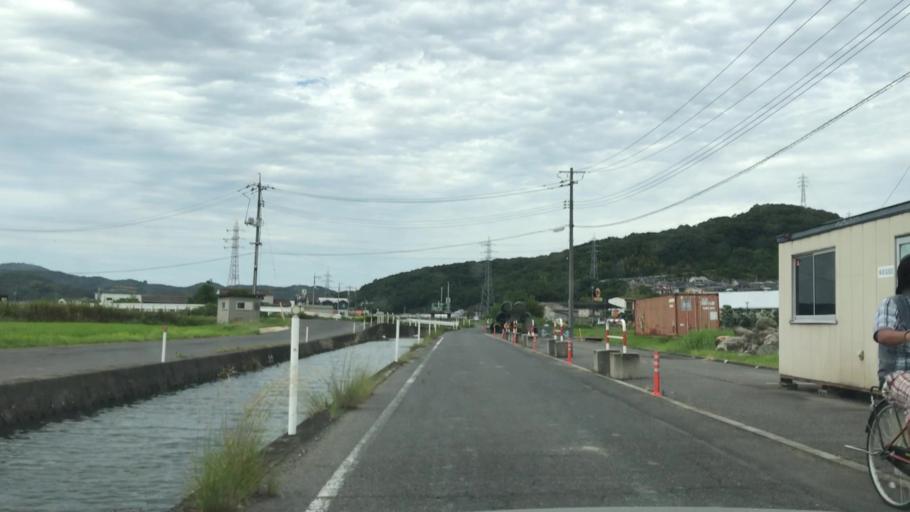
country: JP
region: Okayama
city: Okayama-shi
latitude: 34.6681
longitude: 133.9975
